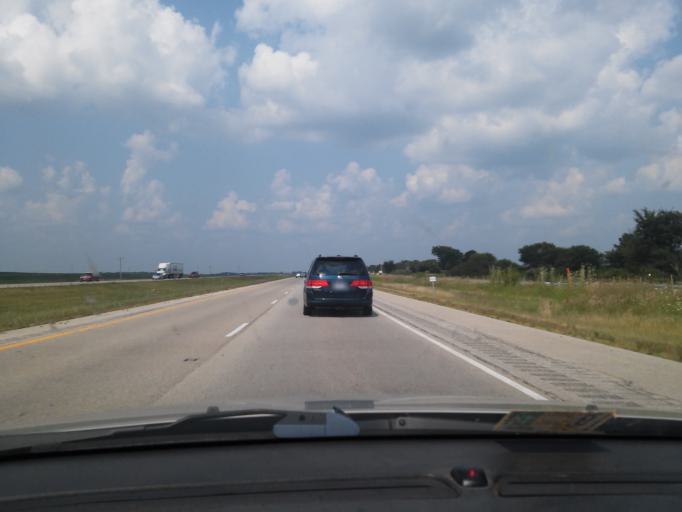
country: US
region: Illinois
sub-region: McLean County
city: Lexington
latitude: 40.6068
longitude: -88.8363
